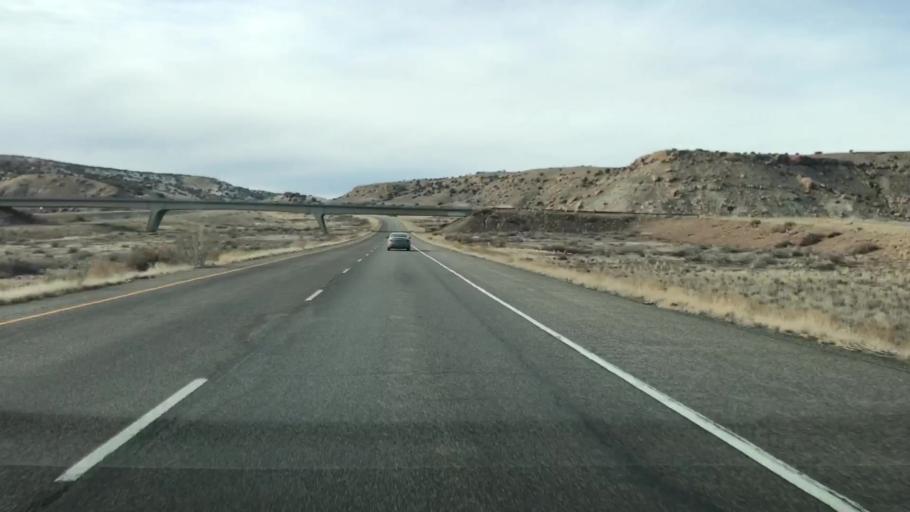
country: US
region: Colorado
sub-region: Mesa County
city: Loma
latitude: 39.1914
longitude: -109.0166
